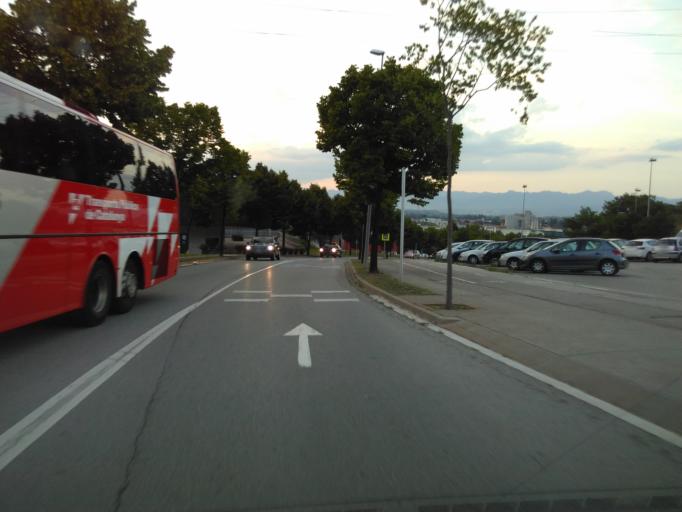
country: ES
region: Catalonia
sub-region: Provincia de Barcelona
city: Vic
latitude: 41.9357
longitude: 2.2498
